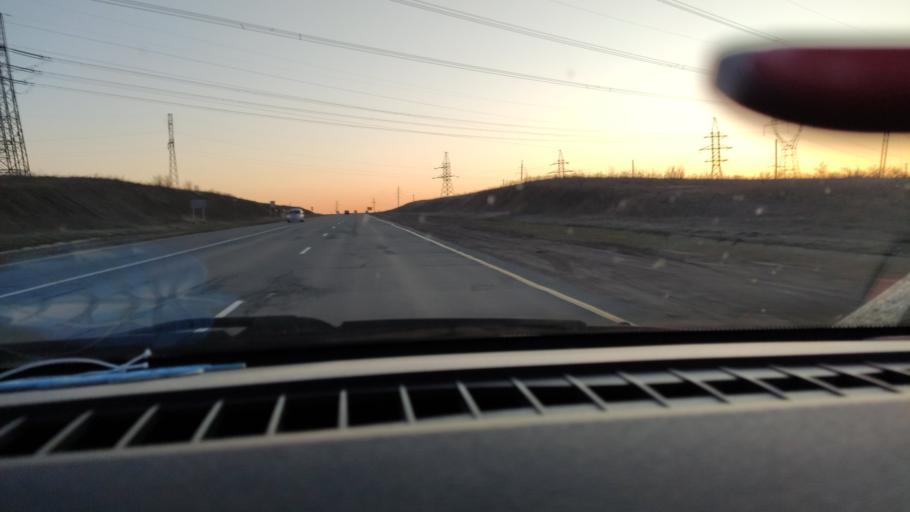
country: RU
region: Saratov
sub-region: Saratovskiy Rayon
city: Saratov
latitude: 51.7652
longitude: 46.0769
